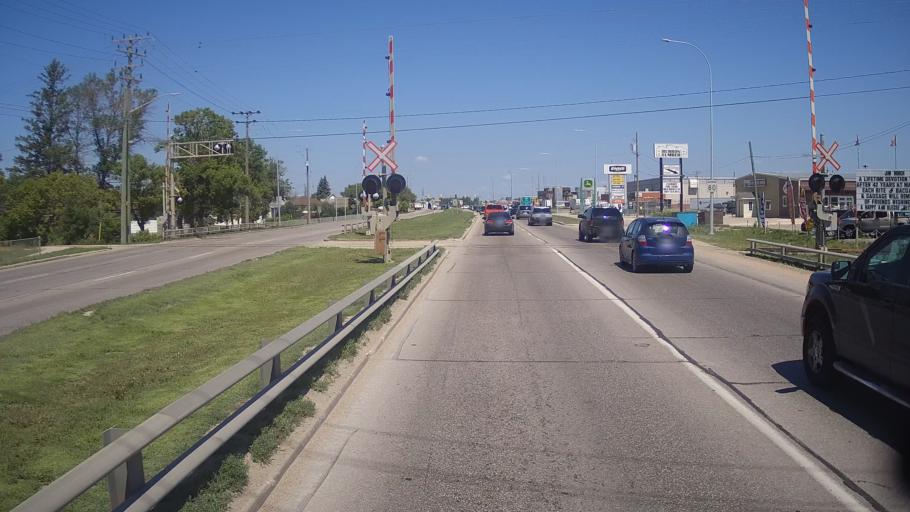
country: CA
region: Manitoba
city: Winnipeg
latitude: 49.8825
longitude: -97.0721
